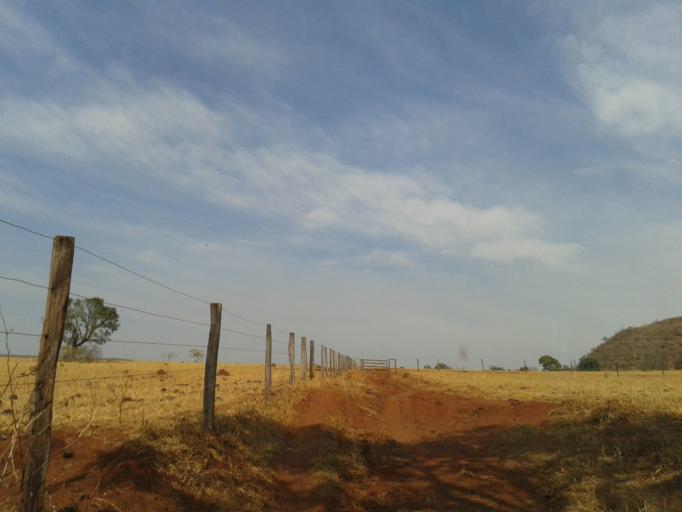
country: BR
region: Minas Gerais
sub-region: Santa Vitoria
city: Santa Vitoria
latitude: -19.2266
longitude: -50.0229
